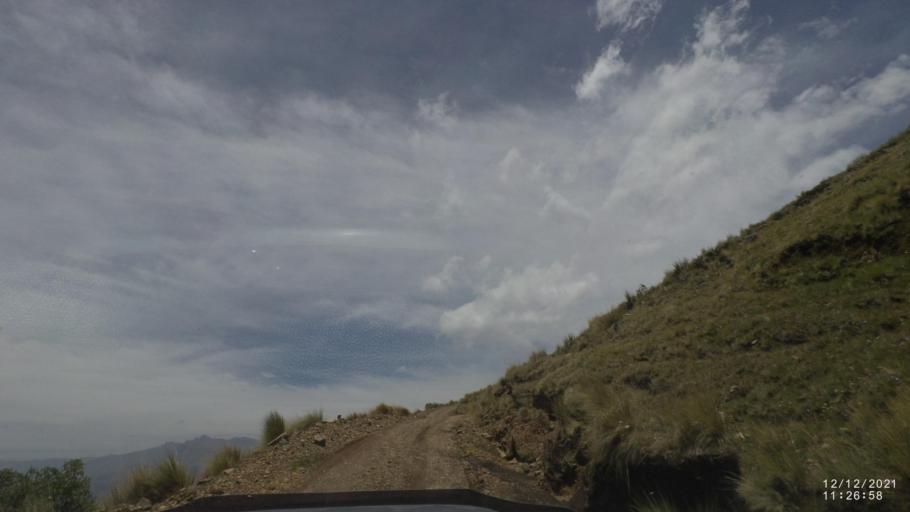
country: BO
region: Cochabamba
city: Cochabamba
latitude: -17.2972
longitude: -66.1851
